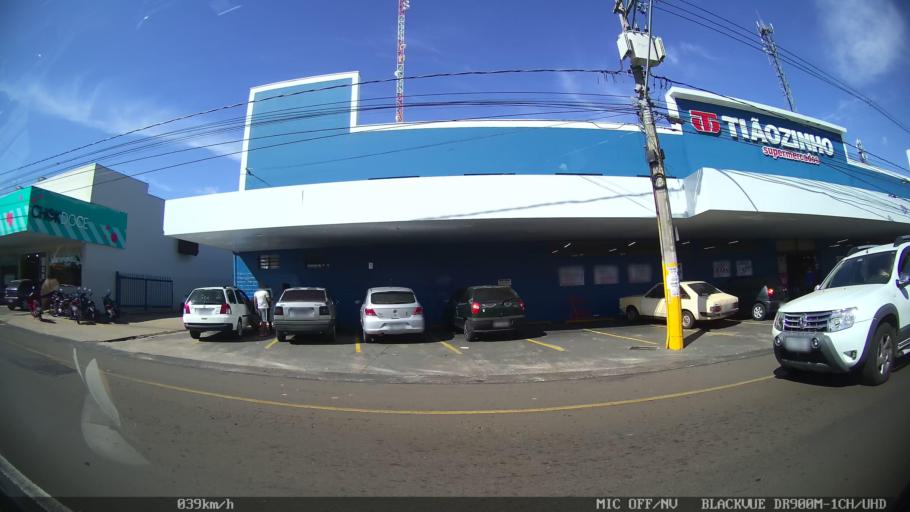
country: BR
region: Sao Paulo
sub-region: Franca
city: Franca
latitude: -20.5191
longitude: -47.4084
